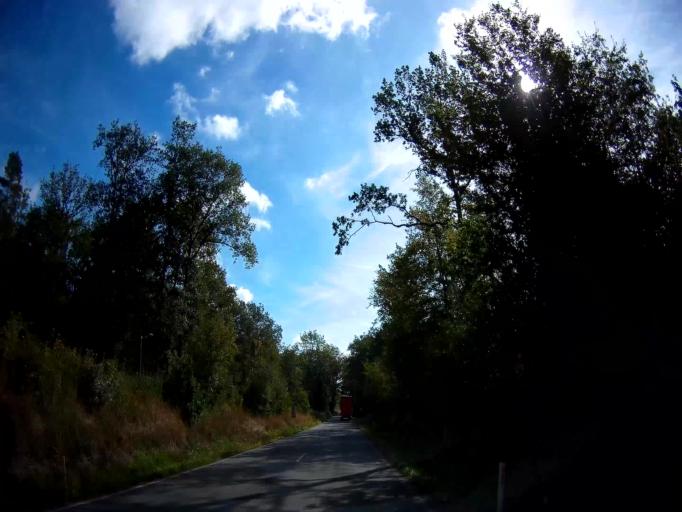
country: BE
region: Wallonia
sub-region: Province de Namur
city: Rochefort
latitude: 50.1674
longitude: 5.1759
